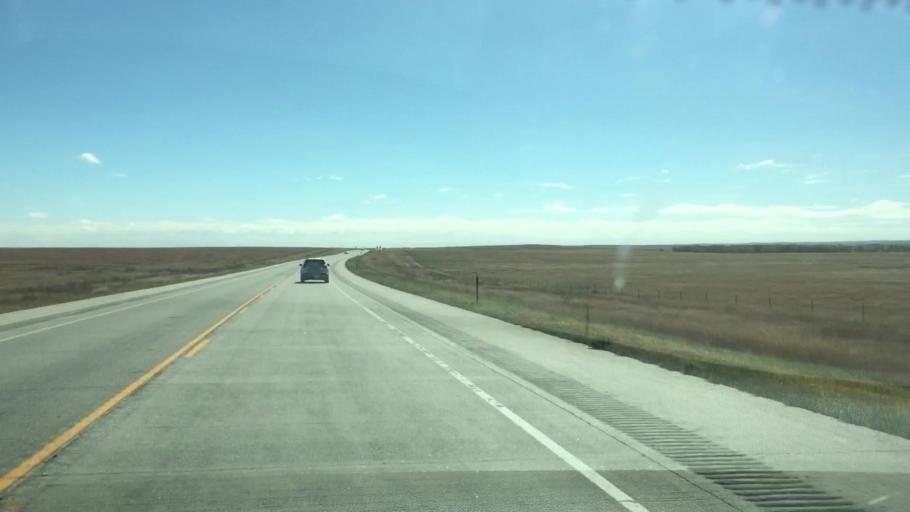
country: US
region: Colorado
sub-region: Lincoln County
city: Hugo
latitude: 39.1914
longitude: -103.5628
